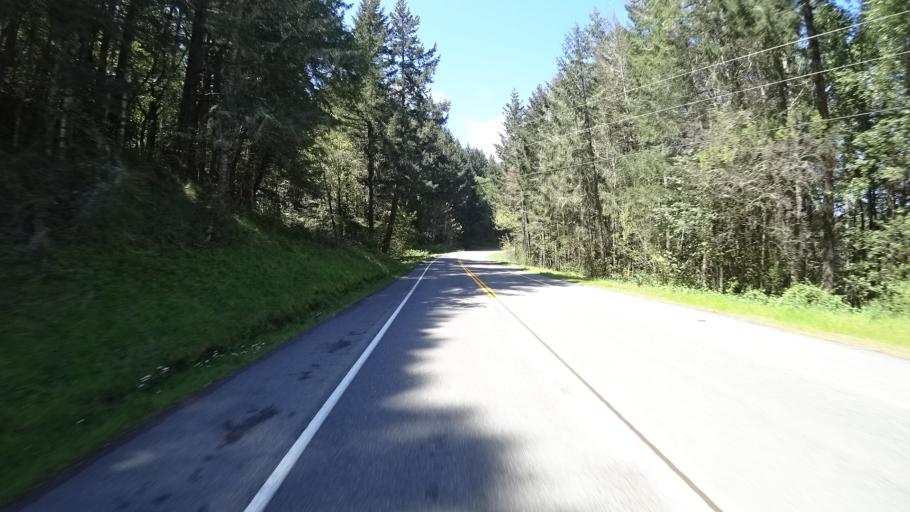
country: US
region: California
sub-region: Humboldt County
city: Blue Lake
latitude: 40.9167
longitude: -123.8305
